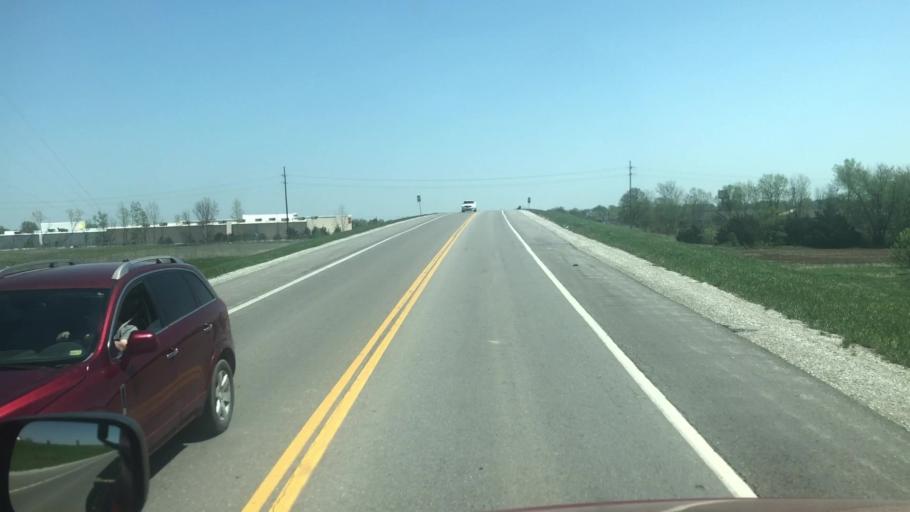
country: US
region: Missouri
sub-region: Adair County
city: Kirksville
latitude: 40.2165
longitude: -92.5894
